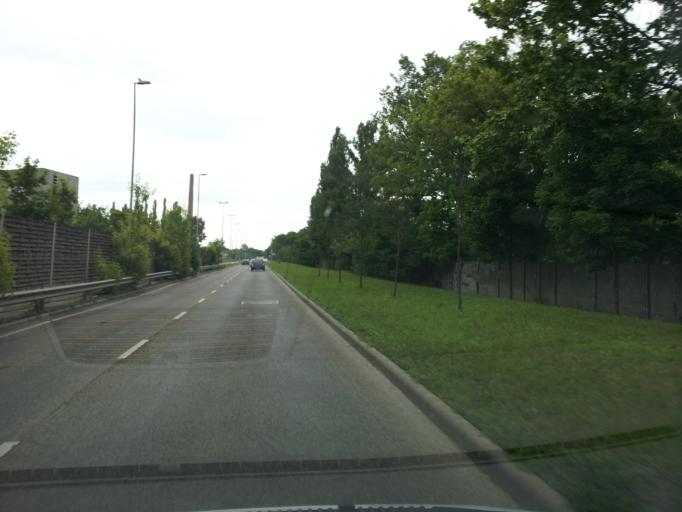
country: HU
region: Budapest
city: Budapest III. keruelet
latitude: 47.5547
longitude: 19.0491
